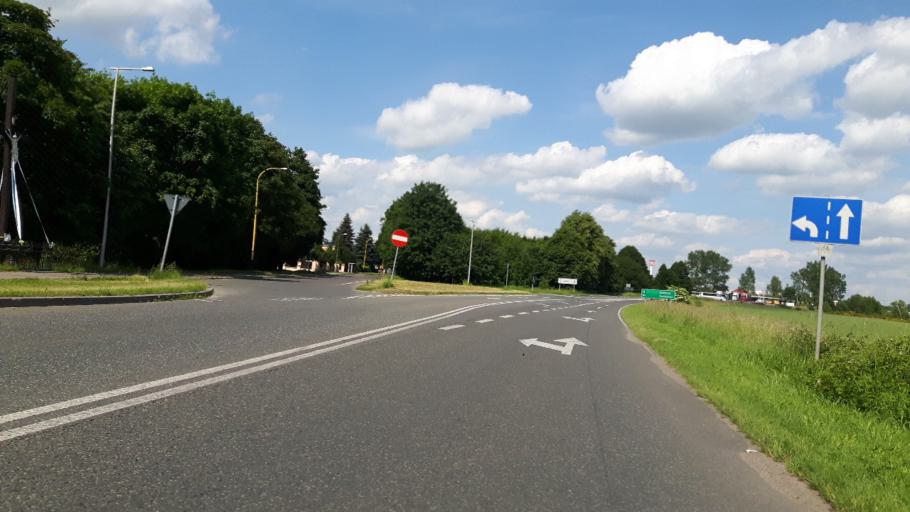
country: PL
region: West Pomeranian Voivodeship
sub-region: Powiat goleniowski
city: Nowogard
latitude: 53.6811
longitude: 15.1186
